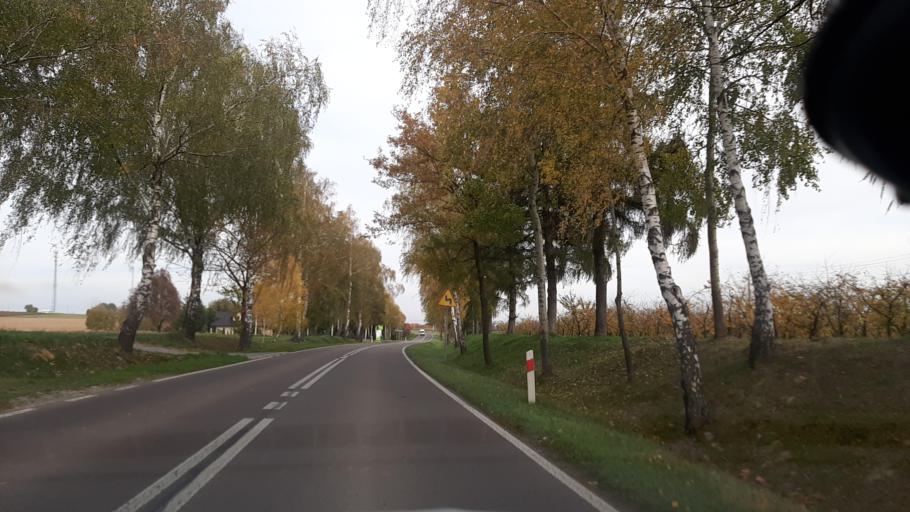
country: PL
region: Lublin Voivodeship
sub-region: Powiat pulawski
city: Markuszow
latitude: 51.3321
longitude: 22.2490
